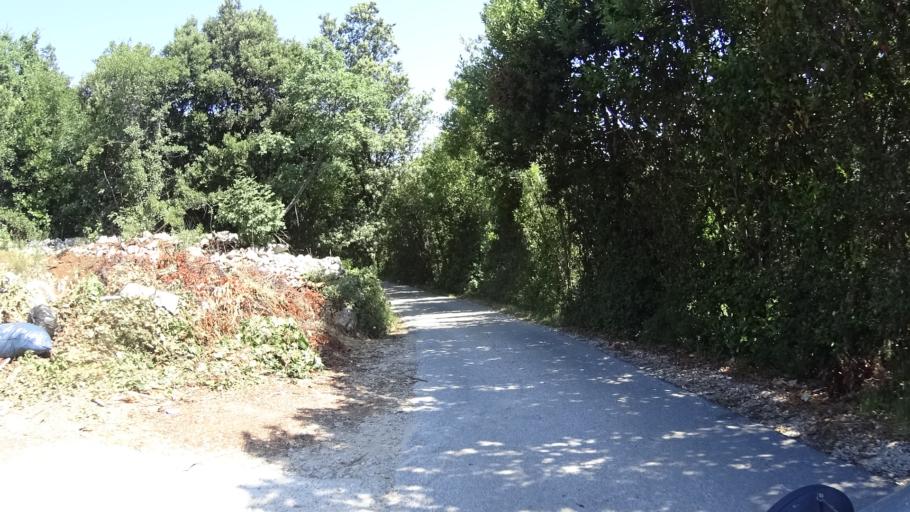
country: HR
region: Istarska
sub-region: Grad Labin
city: Rabac
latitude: 44.9935
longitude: 14.1646
